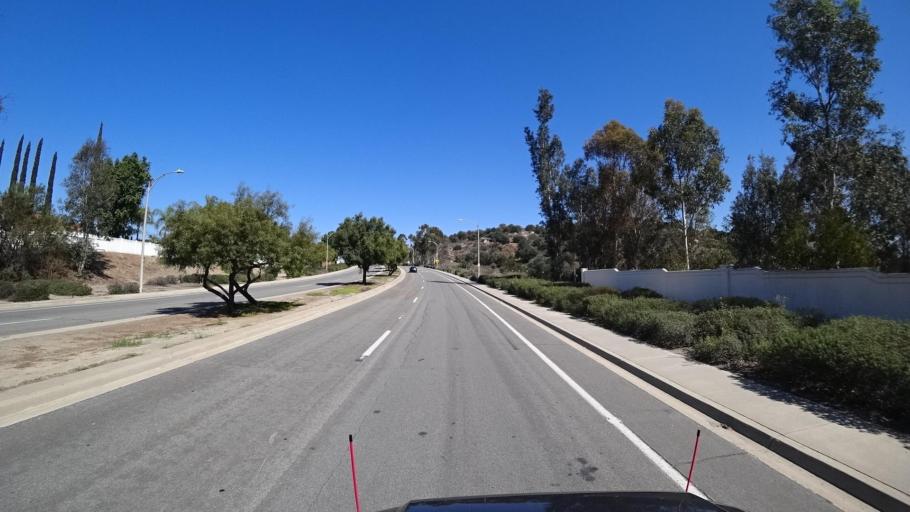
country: US
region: California
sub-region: San Diego County
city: Rancho San Diego
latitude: 32.7519
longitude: -116.9408
